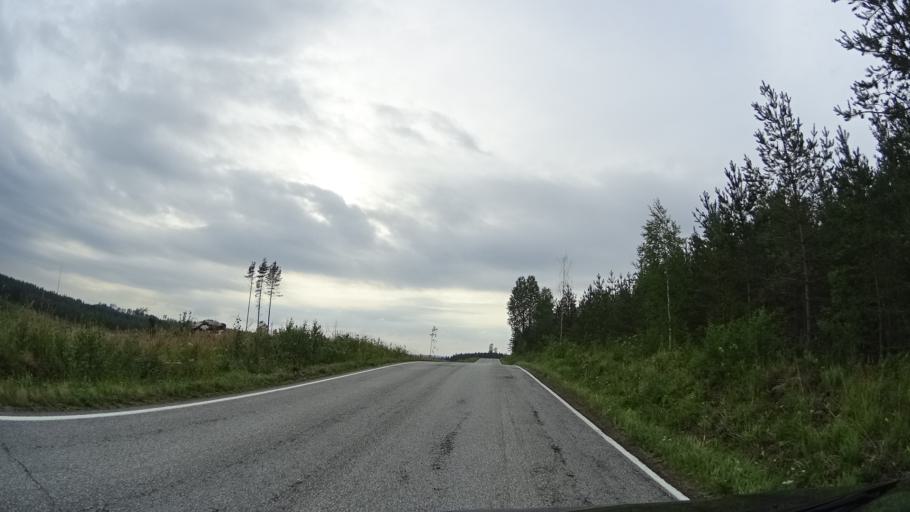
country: FI
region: Southern Savonia
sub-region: Savonlinna
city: Punkaharju
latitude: 61.7513
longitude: 29.4671
